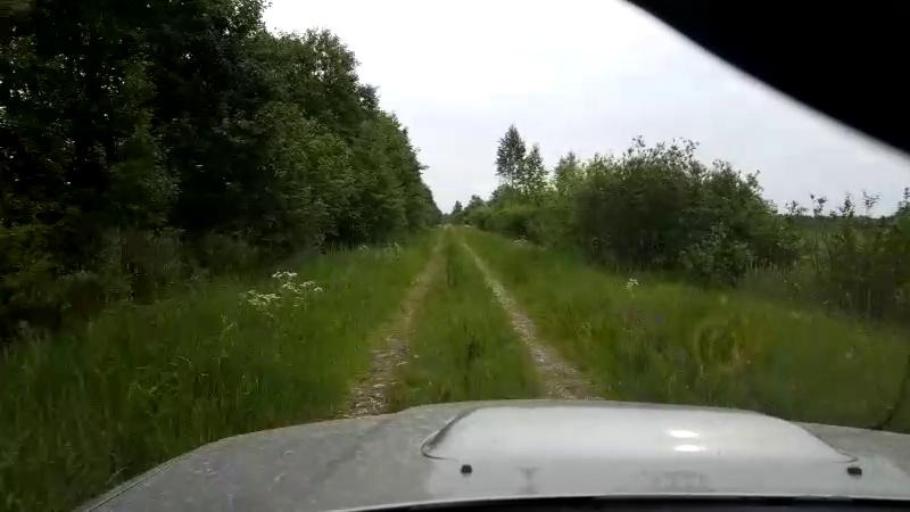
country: EE
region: Paernumaa
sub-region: Tootsi vald
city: Tootsi
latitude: 58.5649
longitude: 24.6890
